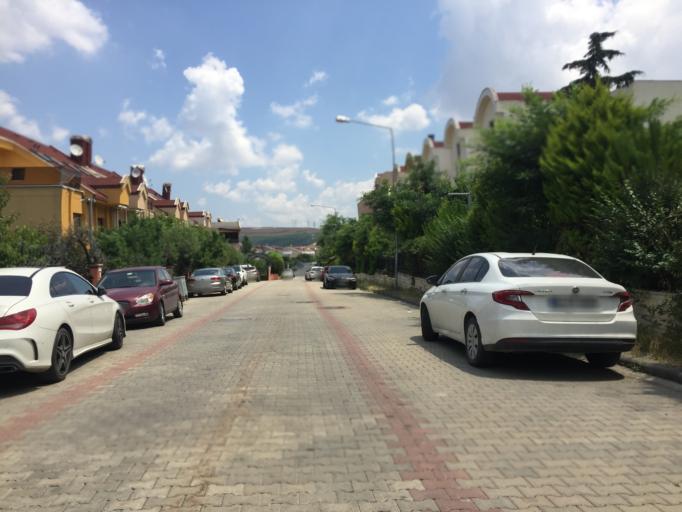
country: TR
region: Istanbul
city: Esenyurt
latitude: 41.0817
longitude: 28.6687
